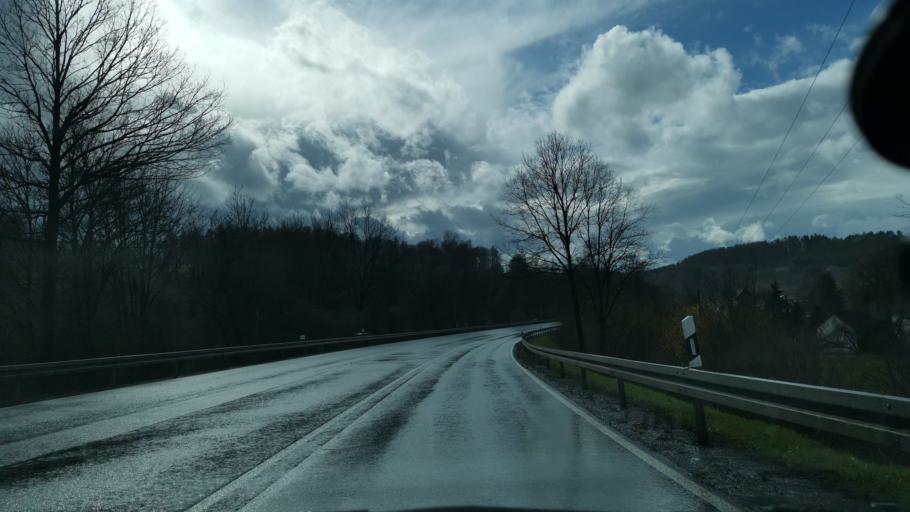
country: DE
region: Hesse
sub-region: Regierungsbezirk Kassel
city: Cornberg
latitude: 51.0245
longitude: 9.8363
